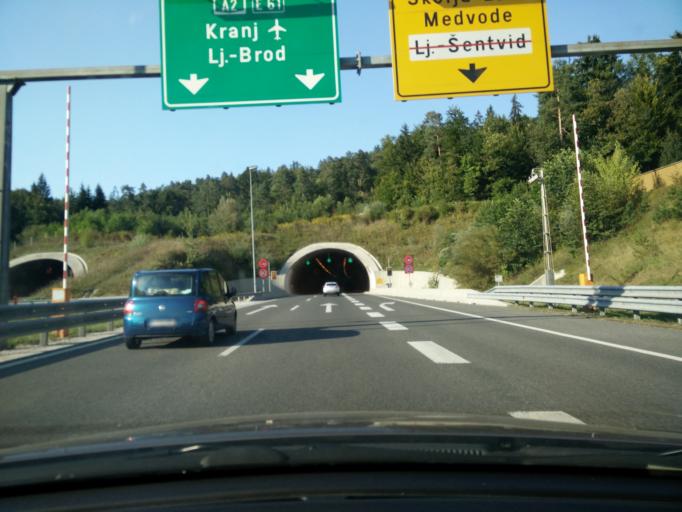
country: SI
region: Ljubljana
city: Ljubljana
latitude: 46.0874
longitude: 14.4605
